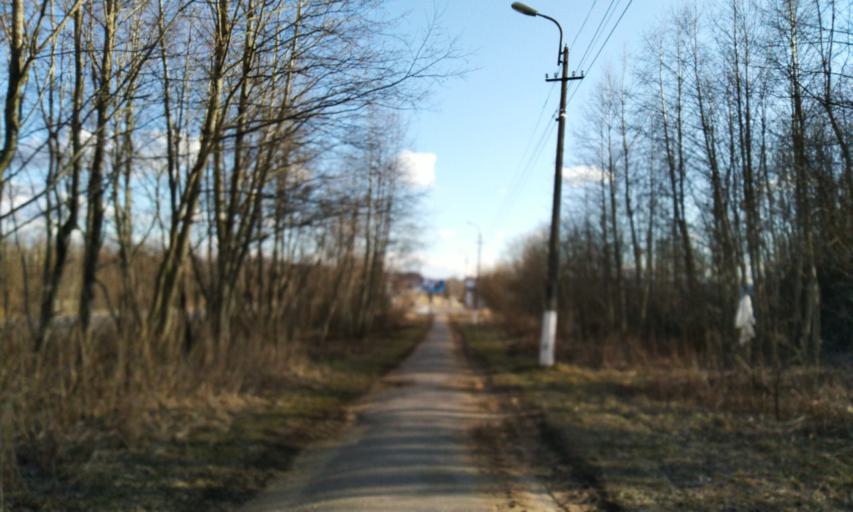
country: RU
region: Leningrad
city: Novoye Devyatkino
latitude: 60.1057
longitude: 30.4995
